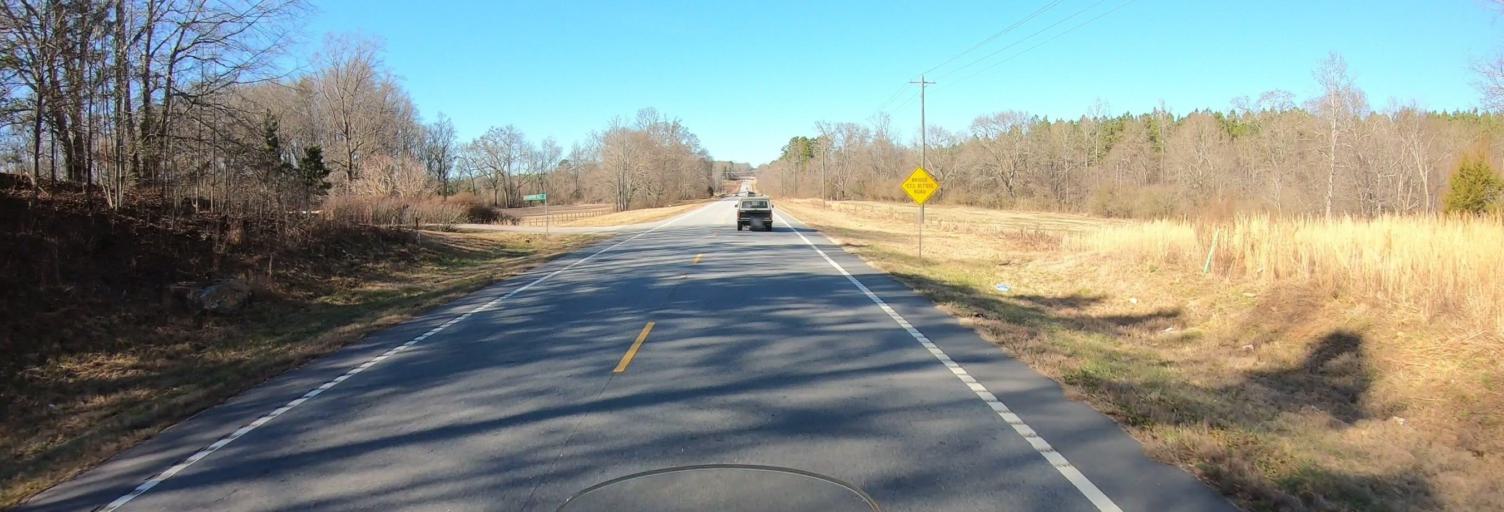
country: US
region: South Carolina
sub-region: Oconee County
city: Walhalla
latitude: 34.7906
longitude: -83.0267
